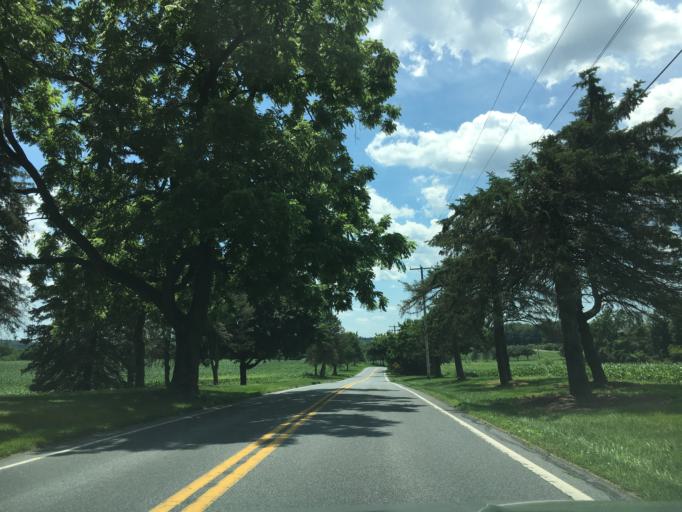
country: US
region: Pennsylvania
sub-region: Lehigh County
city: Schnecksville
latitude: 40.6393
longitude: -75.5774
